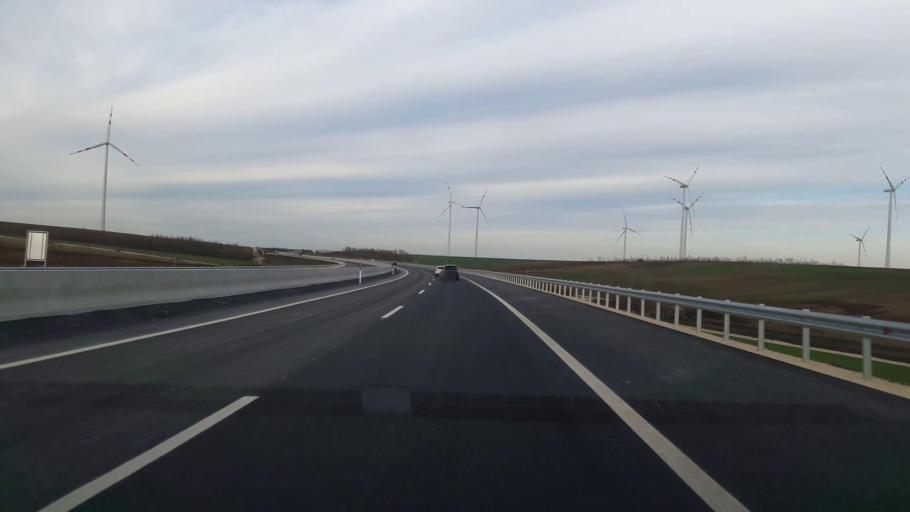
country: AT
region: Lower Austria
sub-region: Politischer Bezirk Mistelbach
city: Wilfersdorf
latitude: 48.6152
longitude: 16.6763
